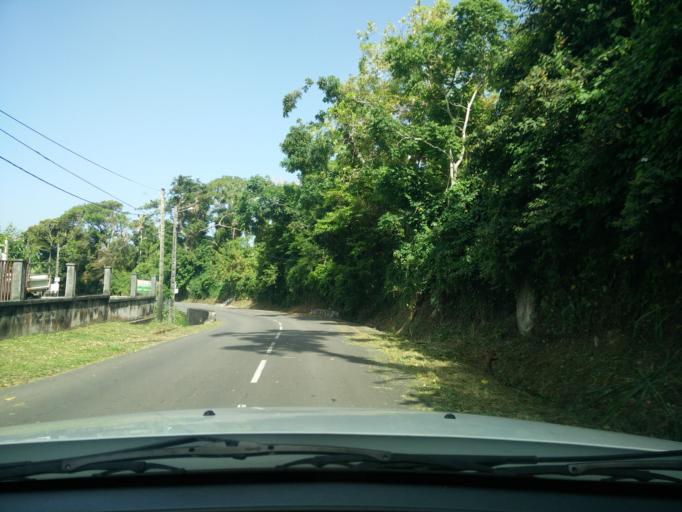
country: GP
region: Guadeloupe
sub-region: Guadeloupe
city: Gourbeyre
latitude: 15.9992
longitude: -61.6997
